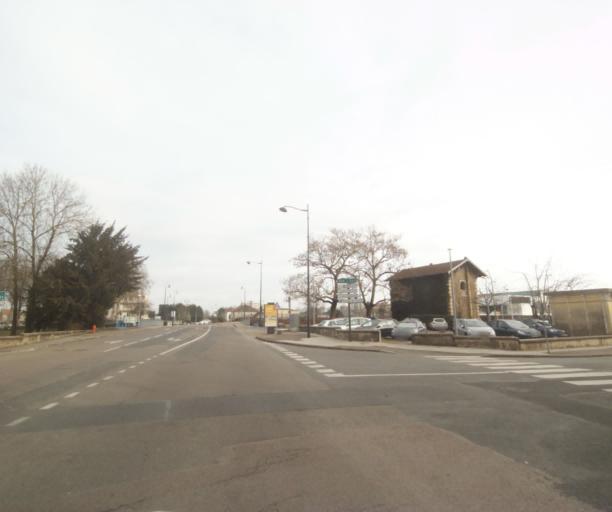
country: FR
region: Champagne-Ardenne
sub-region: Departement de la Haute-Marne
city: Saint-Dizier
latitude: 48.6407
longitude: 4.9482
